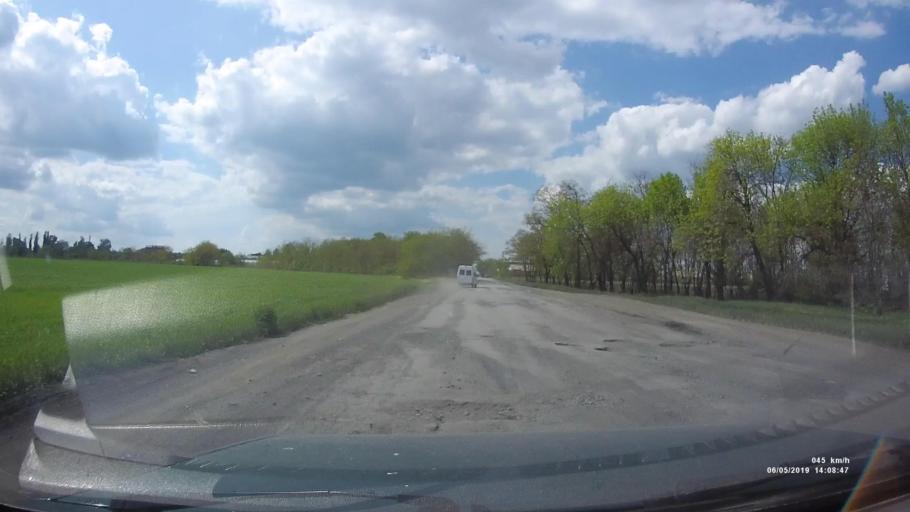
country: RU
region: Rostov
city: Shakhty
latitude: 47.6844
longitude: 40.2950
